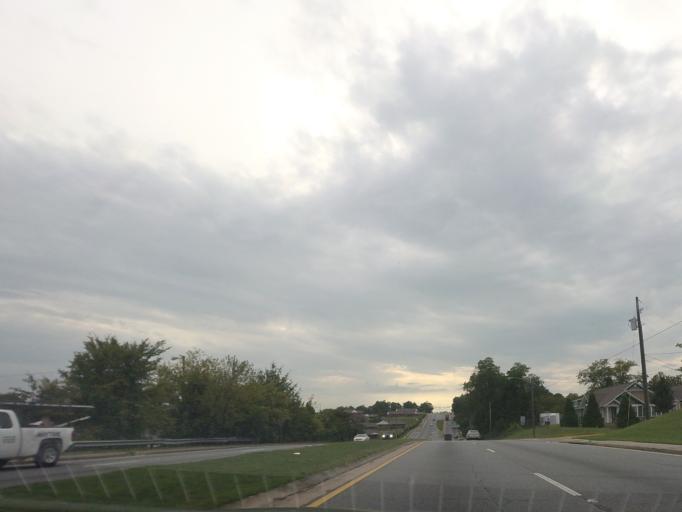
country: US
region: Georgia
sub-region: Bibb County
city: Macon
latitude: 32.8482
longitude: -83.6055
